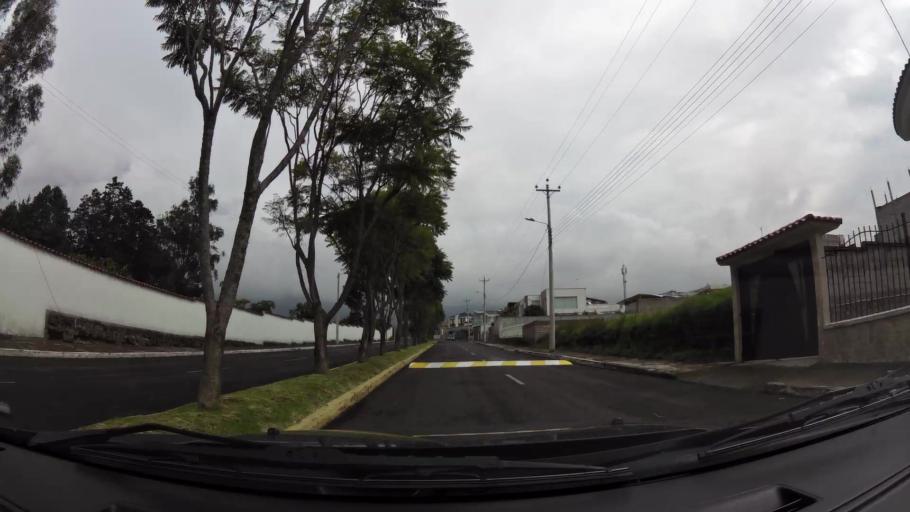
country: EC
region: Pichincha
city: Sangolqui
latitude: -0.3052
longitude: -78.4781
